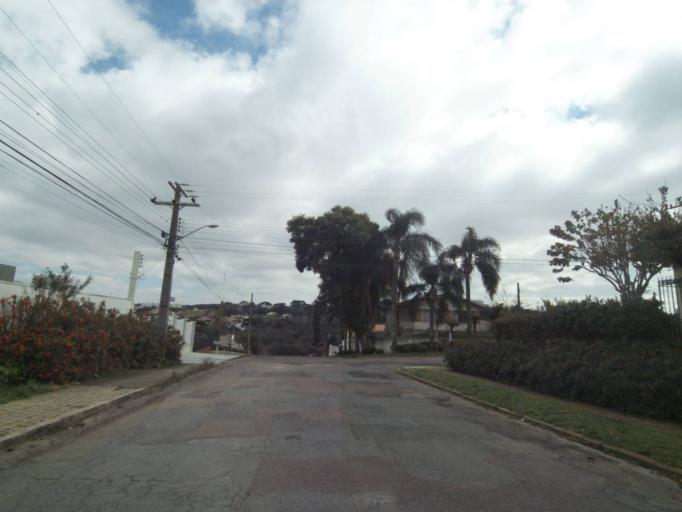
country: BR
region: Parana
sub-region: Curitiba
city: Curitiba
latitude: -25.4510
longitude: -49.3116
